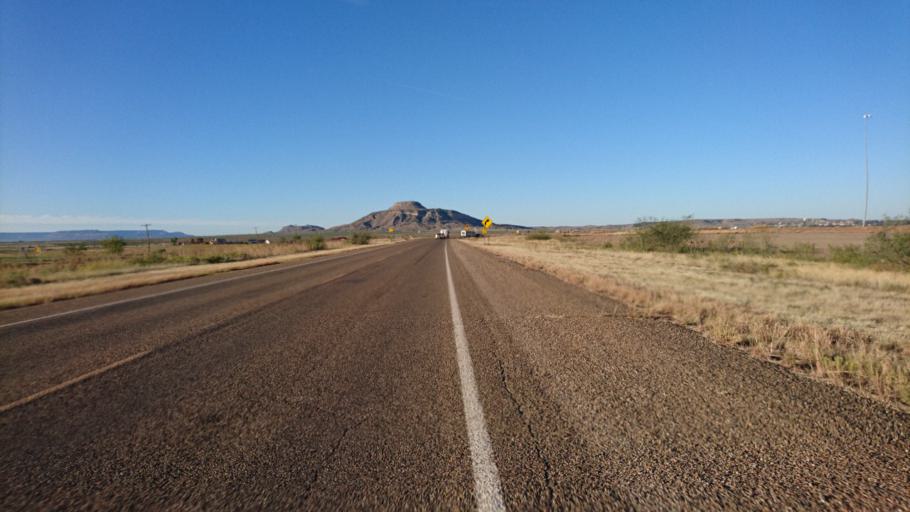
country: US
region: New Mexico
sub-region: Quay County
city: Tucumcari
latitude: 35.1694
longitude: -103.6720
